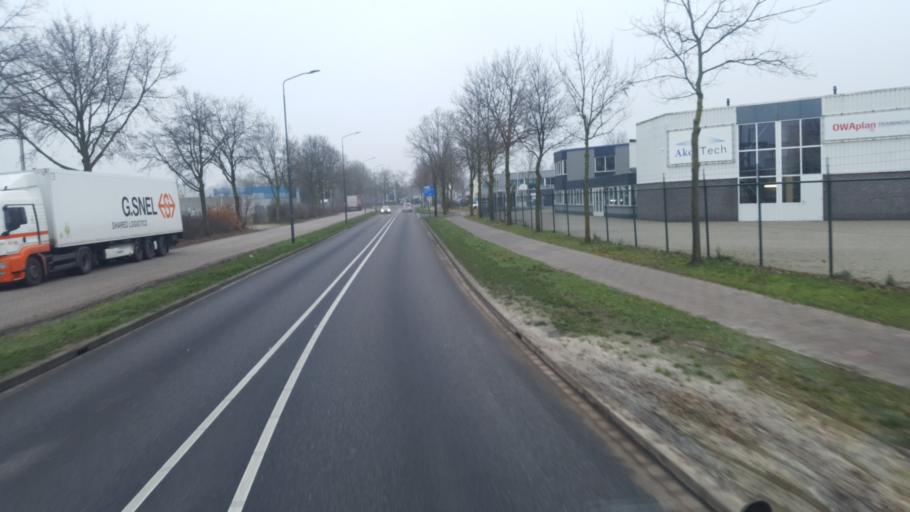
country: NL
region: North Brabant
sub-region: Gemeente Helmond
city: Helmond
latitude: 51.4640
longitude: 5.6899
